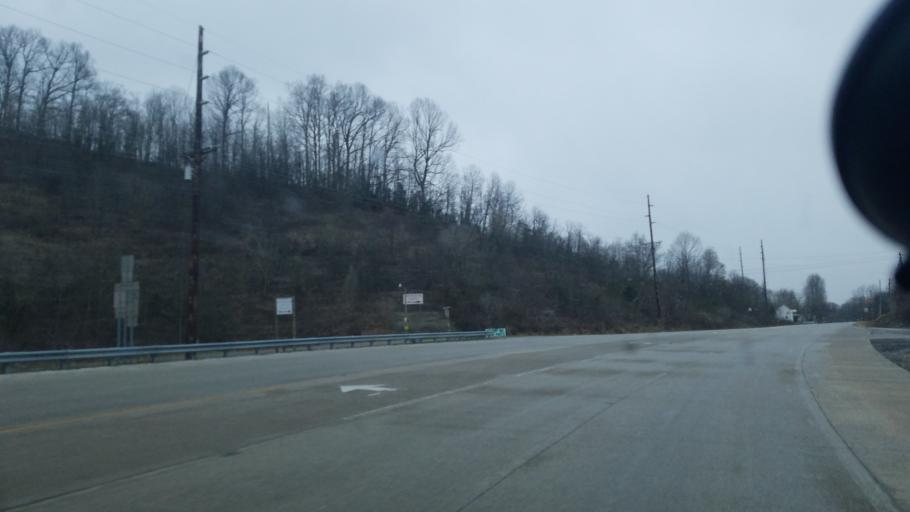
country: US
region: Ohio
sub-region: Scioto County
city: Portsmouth
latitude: 38.7208
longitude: -83.0166
